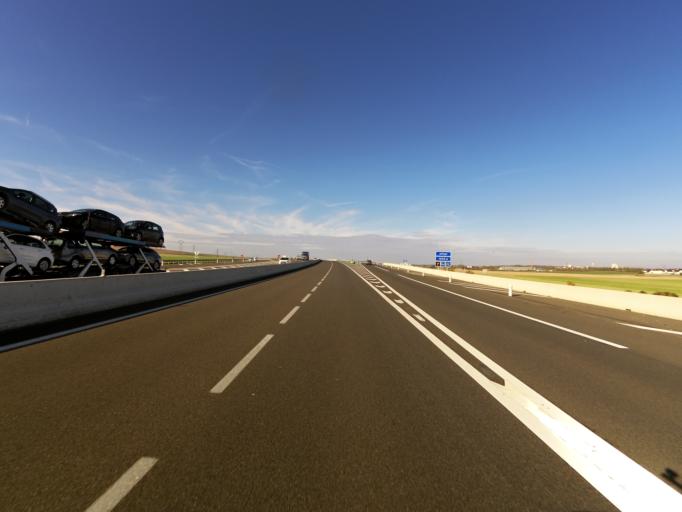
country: FR
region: Champagne-Ardenne
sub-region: Departement de la Marne
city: Taissy
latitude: 49.2050
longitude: 4.0896
